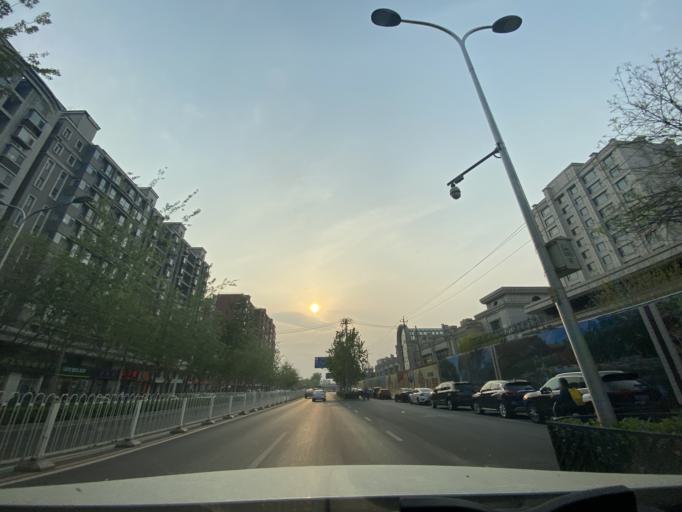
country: CN
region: Beijing
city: Babaoshan
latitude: 39.9284
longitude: 116.2358
